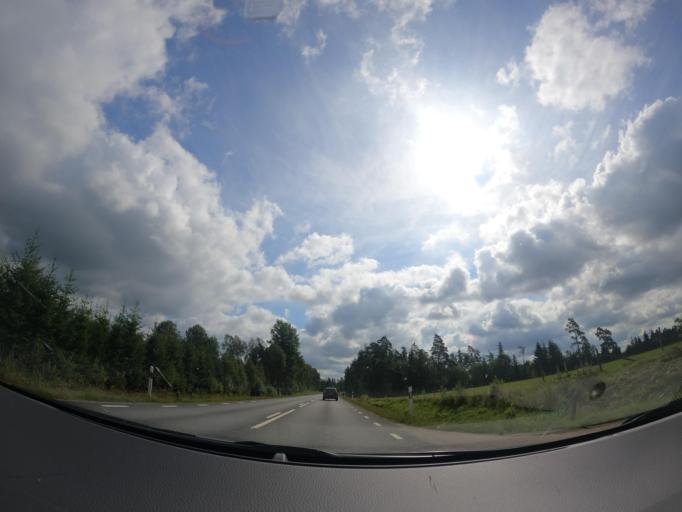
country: SE
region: Joenkoeping
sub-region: Gislaveds Kommun
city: Smalandsstenar
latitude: 57.1204
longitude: 13.3752
